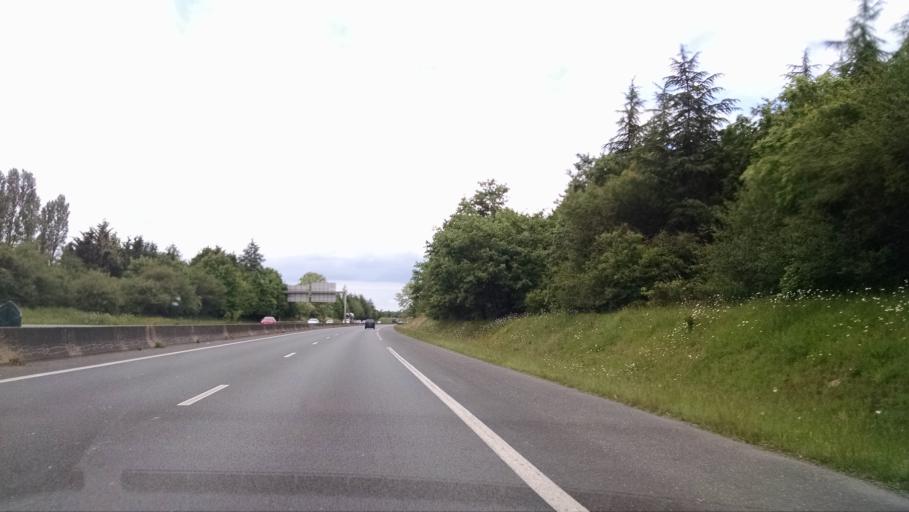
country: FR
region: Pays de la Loire
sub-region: Departement de la Loire-Atlantique
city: Les Sorinieres
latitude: 47.1396
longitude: -1.5129
